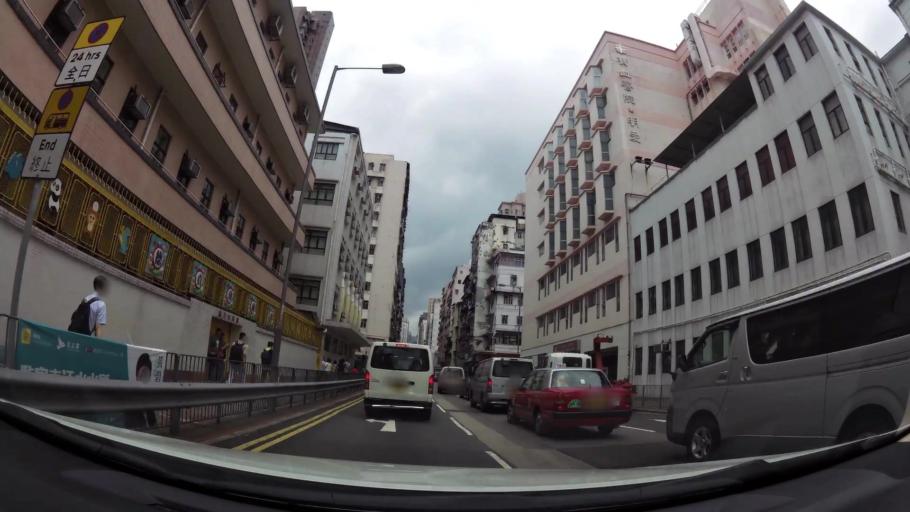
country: HK
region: Sham Shui Po
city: Sham Shui Po
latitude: 22.3335
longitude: 114.1617
